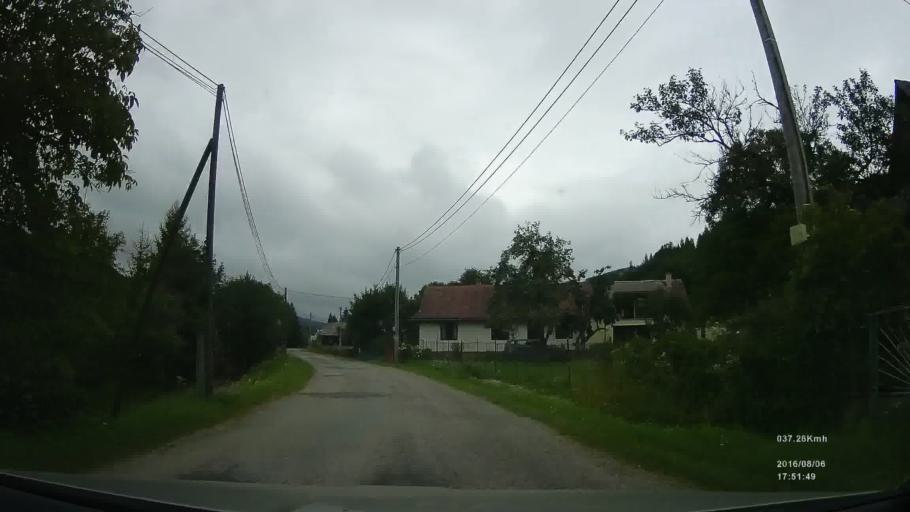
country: SK
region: Presovsky
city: Svidnik
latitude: 49.4024
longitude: 21.5697
